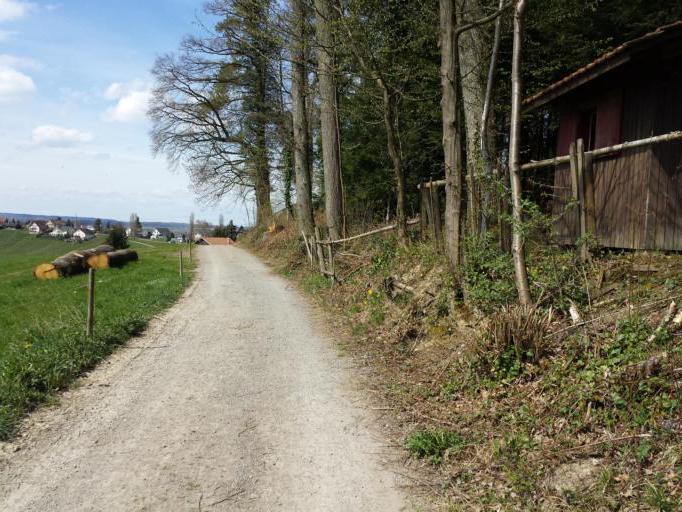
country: CH
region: Saint Gallen
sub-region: Wahlkreis St. Gallen
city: Muolen
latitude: 47.5331
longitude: 9.3132
